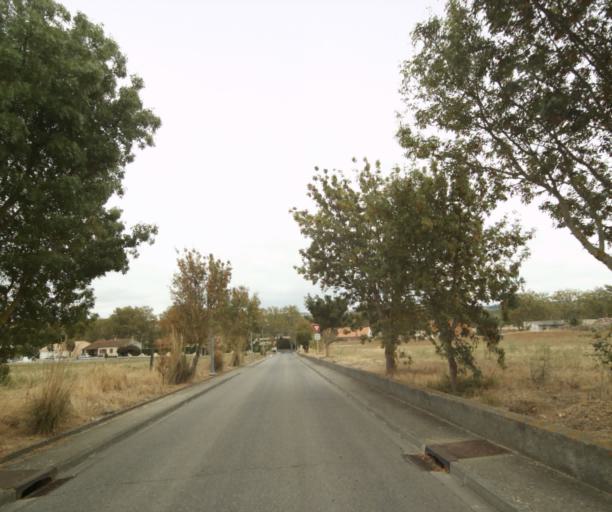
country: FR
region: Midi-Pyrenees
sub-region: Departement de la Haute-Garonne
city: Villefranche-de-Lauragais
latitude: 43.3945
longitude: 1.7243
